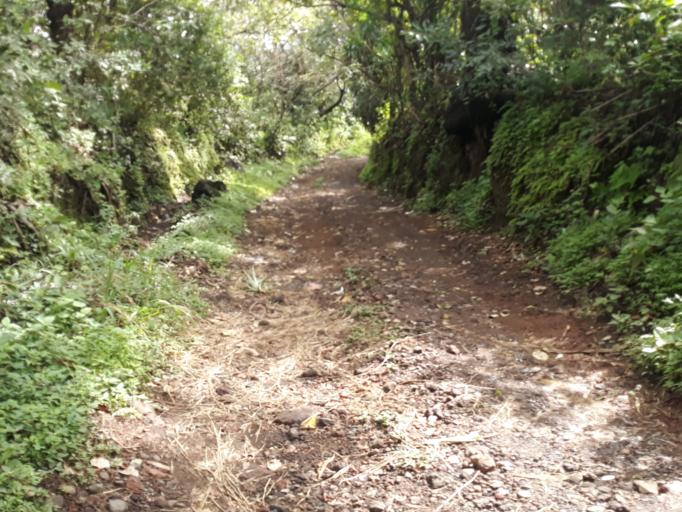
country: GT
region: Escuintla
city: San Vicente Pacaya
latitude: 14.3653
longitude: -90.5531
